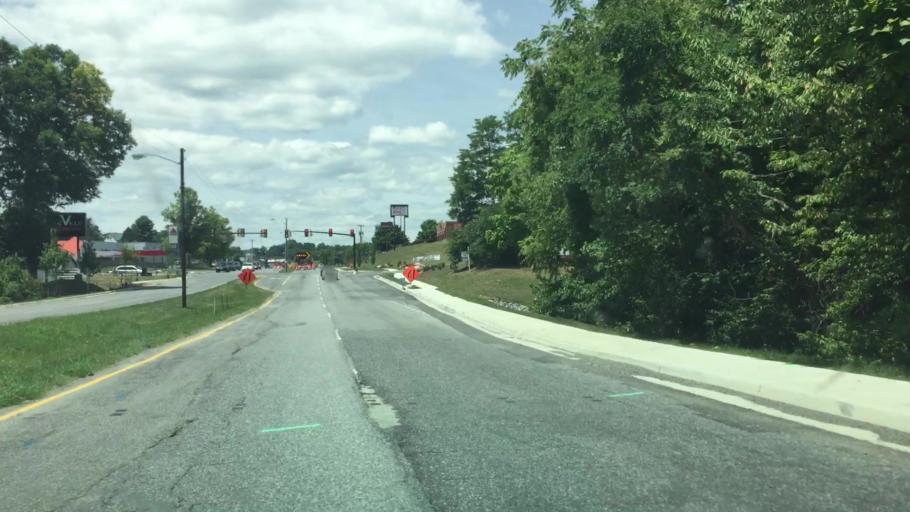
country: US
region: Virginia
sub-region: Wythe County
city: Wytheville
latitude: 36.9486
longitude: -81.0632
